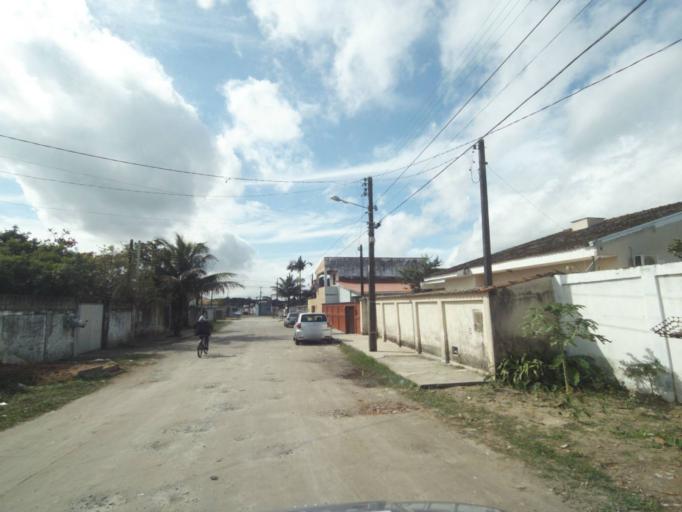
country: BR
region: Parana
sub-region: Paranagua
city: Paranagua
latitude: -25.5673
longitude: -48.5636
